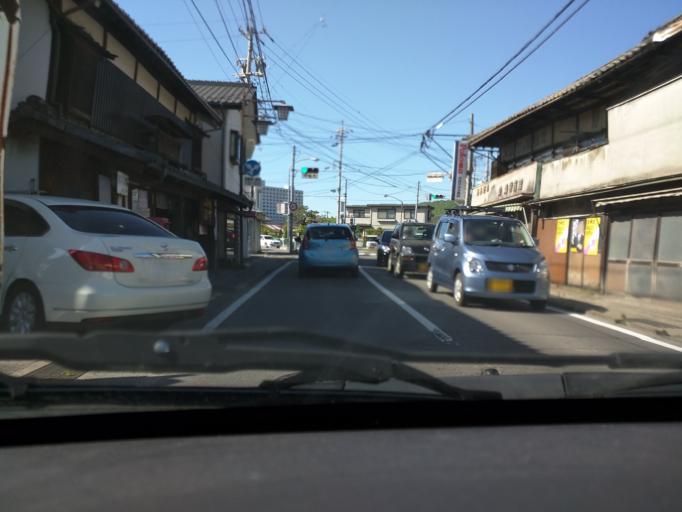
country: JP
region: Nagano
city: Nagano-shi
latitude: 36.5670
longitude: 138.2015
